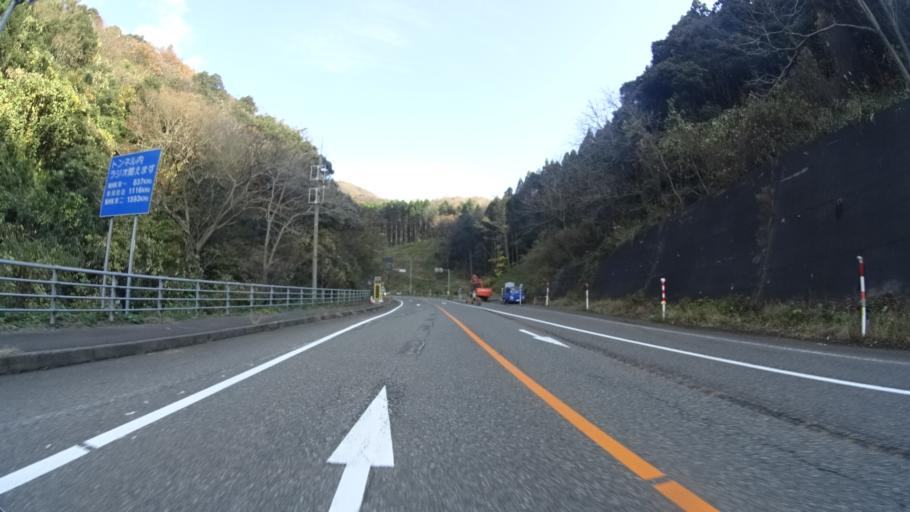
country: JP
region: Niigata
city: Kashiwazaki
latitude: 37.3197
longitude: 138.4399
